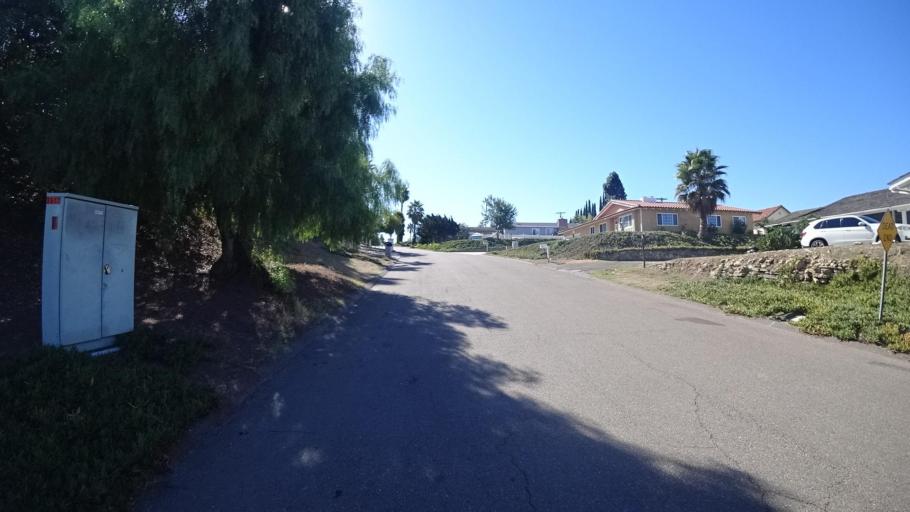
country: US
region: California
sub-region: San Diego County
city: Bonita
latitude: 32.6740
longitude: -117.0168
